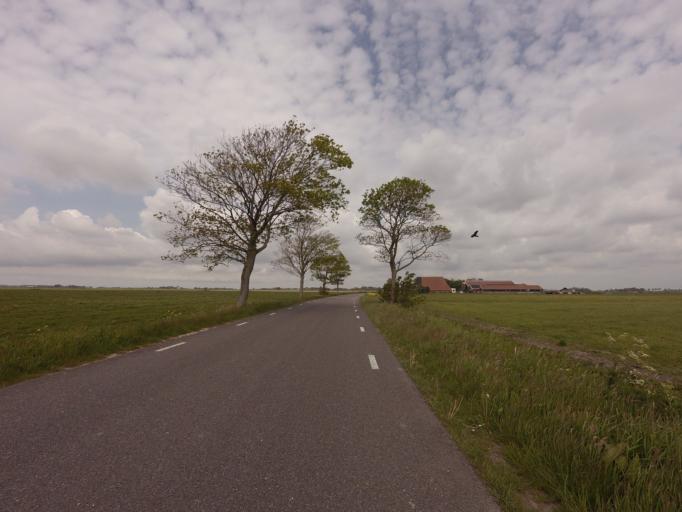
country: NL
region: Friesland
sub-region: Sudwest Fryslan
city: Bolsward
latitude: 53.0964
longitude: 5.5346
